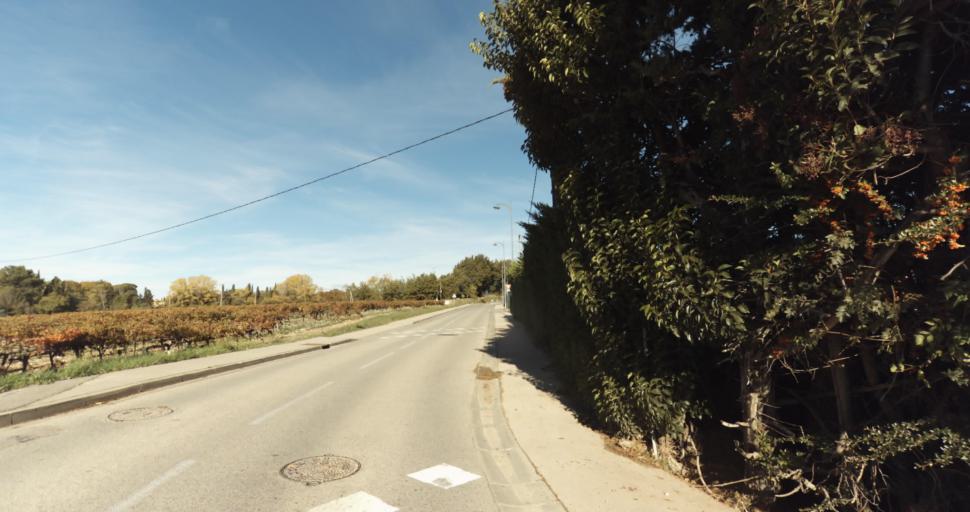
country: FR
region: Provence-Alpes-Cote d'Azur
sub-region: Departement des Bouches-du-Rhone
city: Venelles
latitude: 43.5810
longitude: 5.4667
